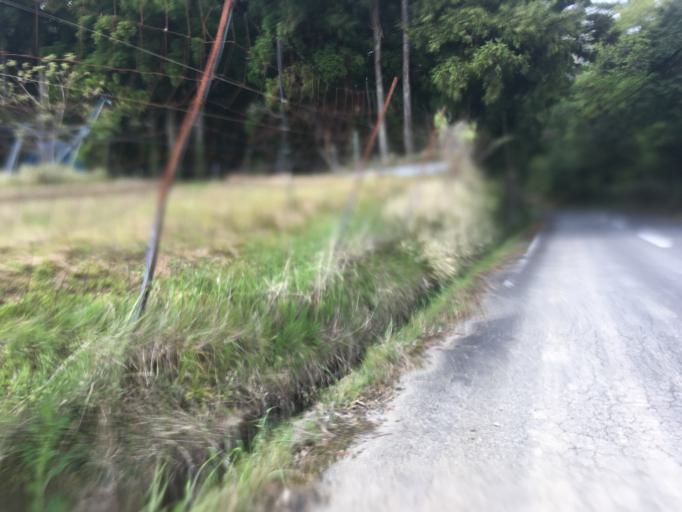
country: JP
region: Kyoto
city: Kameoka
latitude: 35.0902
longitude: 135.6087
